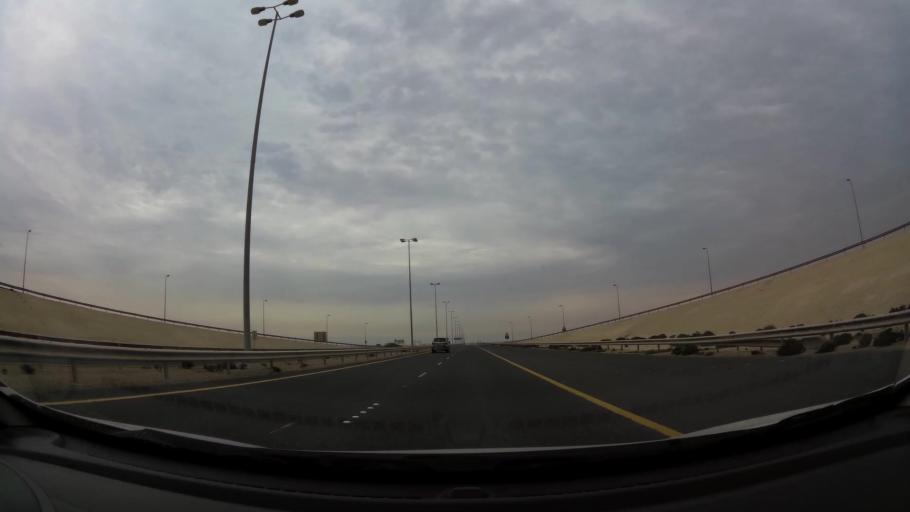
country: BH
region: Central Governorate
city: Dar Kulayb
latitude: 25.8861
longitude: 50.5773
